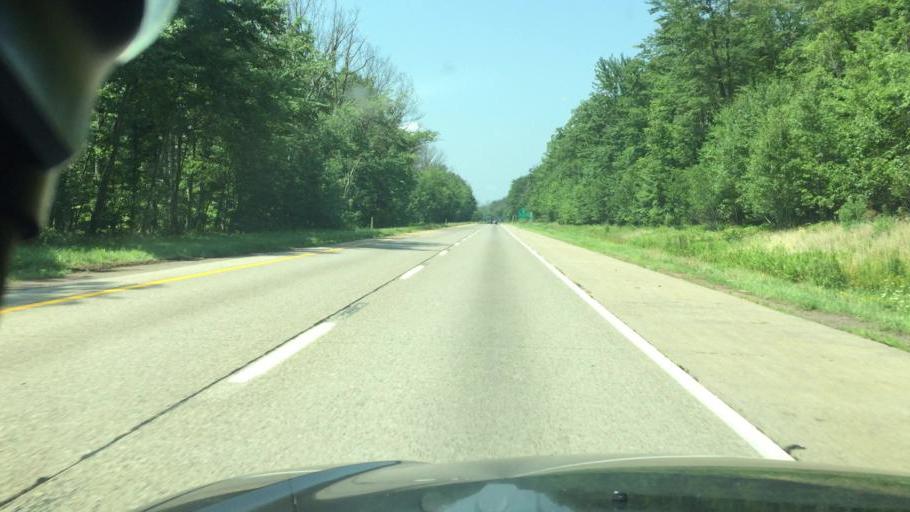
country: US
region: Pennsylvania
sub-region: Luzerne County
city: Conyngham
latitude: 41.0365
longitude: -76.0532
